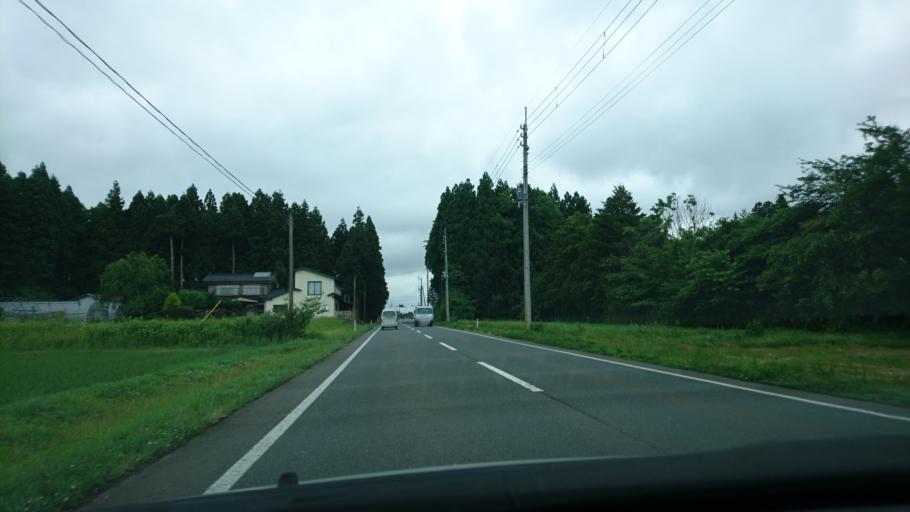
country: JP
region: Iwate
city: Mizusawa
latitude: 39.1168
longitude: 141.0529
